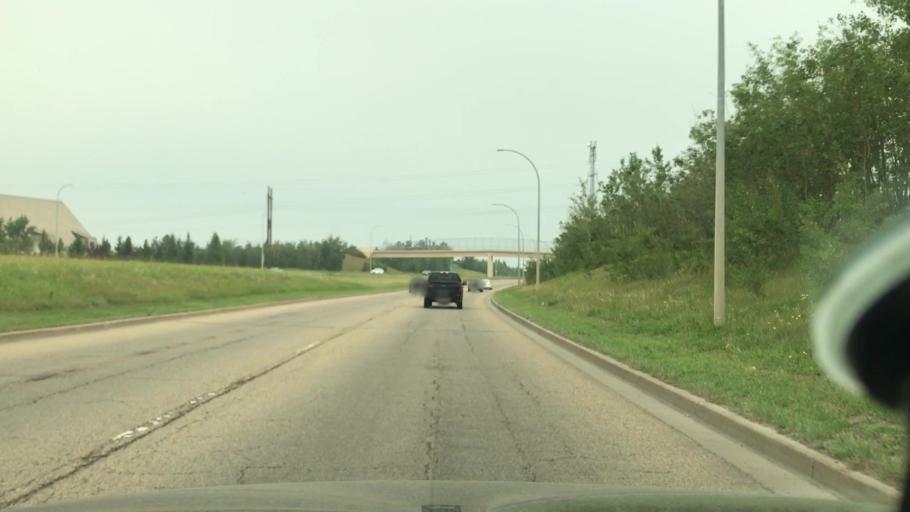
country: CA
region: Alberta
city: Edmonton
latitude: 53.4591
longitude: -113.5878
